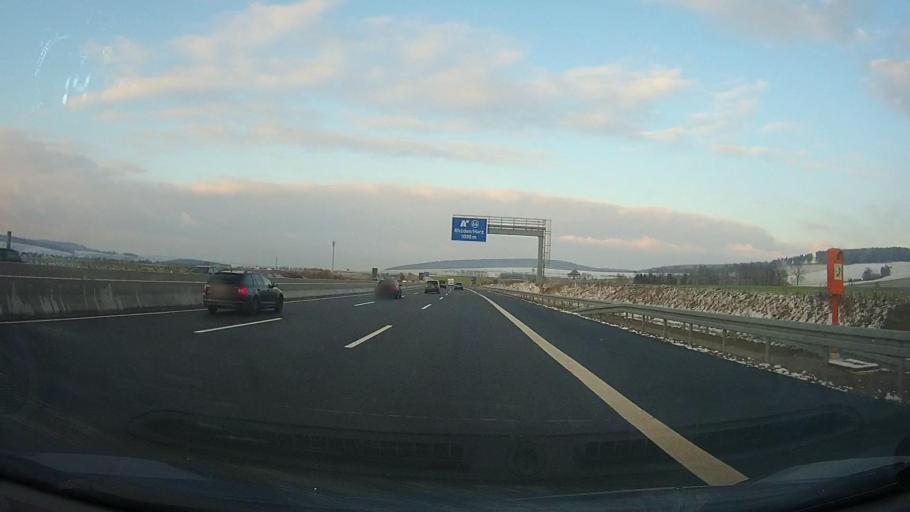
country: DE
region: Lower Saxony
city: Seesen
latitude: 51.9337
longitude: 10.1454
